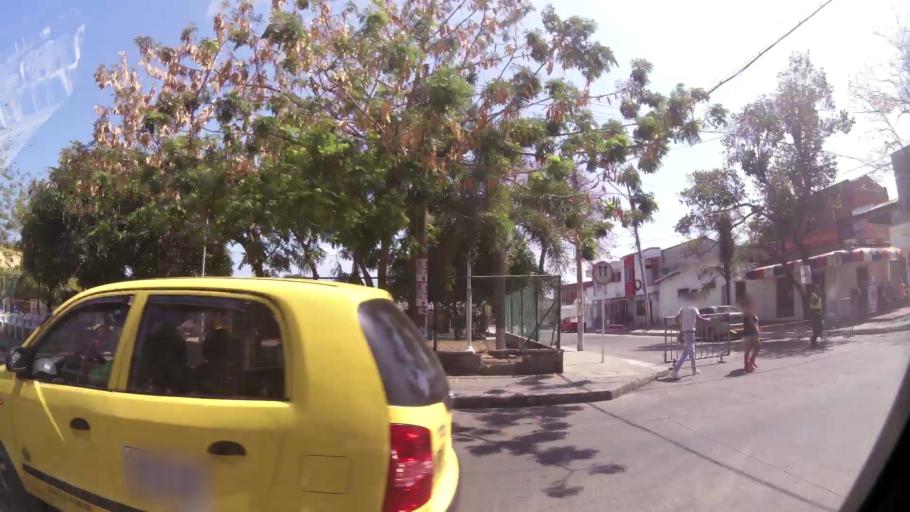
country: CO
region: Atlantico
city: Barranquilla
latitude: 10.9727
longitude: -74.8106
